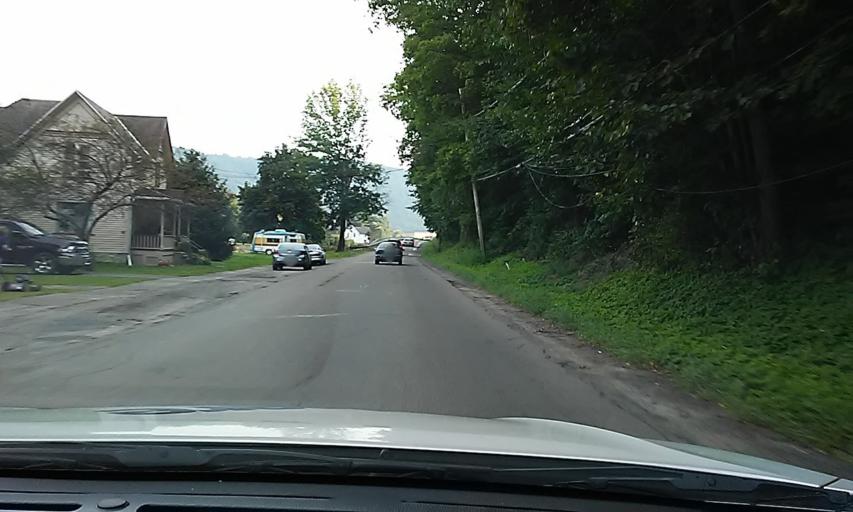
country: US
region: Pennsylvania
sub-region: Potter County
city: Coudersport
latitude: 41.7724
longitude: -78.0239
